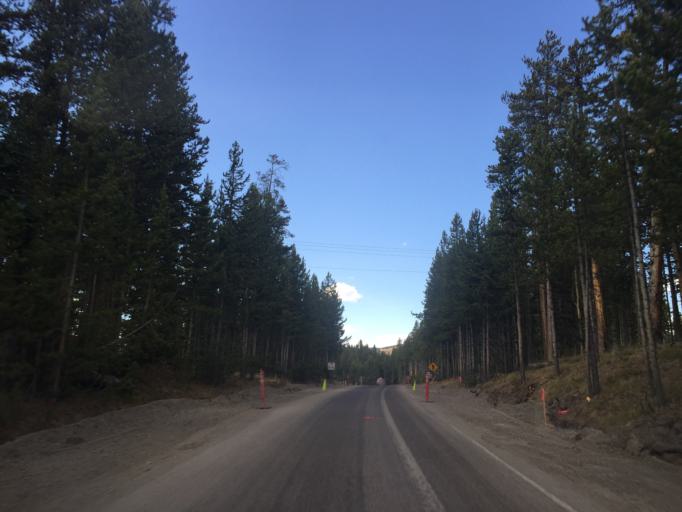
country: US
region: Montana
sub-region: Gallatin County
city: West Yellowstone
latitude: 44.7346
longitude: -110.4877
